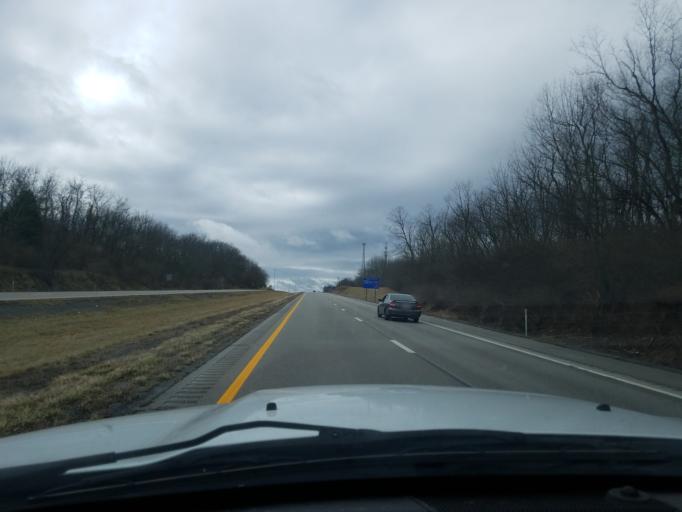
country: US
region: Kentucky
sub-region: Montgomery County
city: Mount Sterling
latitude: 38.0823
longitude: -83.9354
